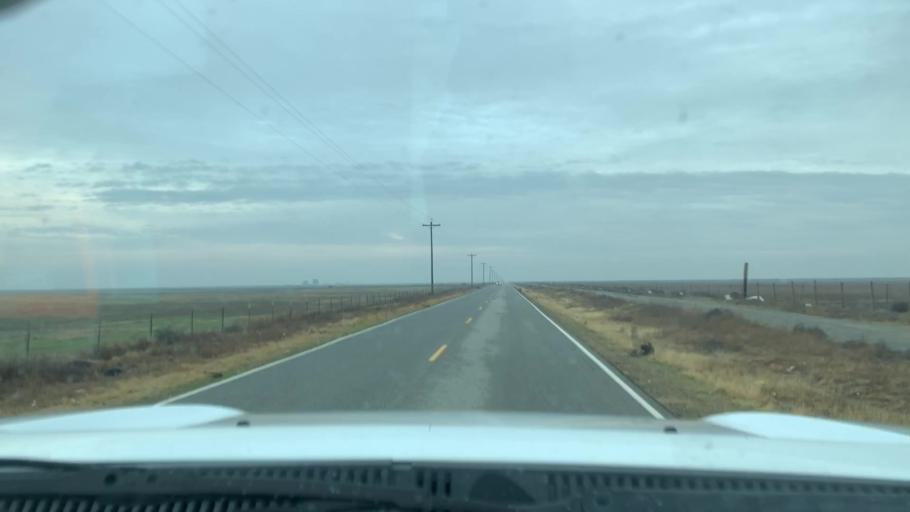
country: US
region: California
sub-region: Kern County
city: Lost Hills
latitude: 35.6670
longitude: -119.5799
